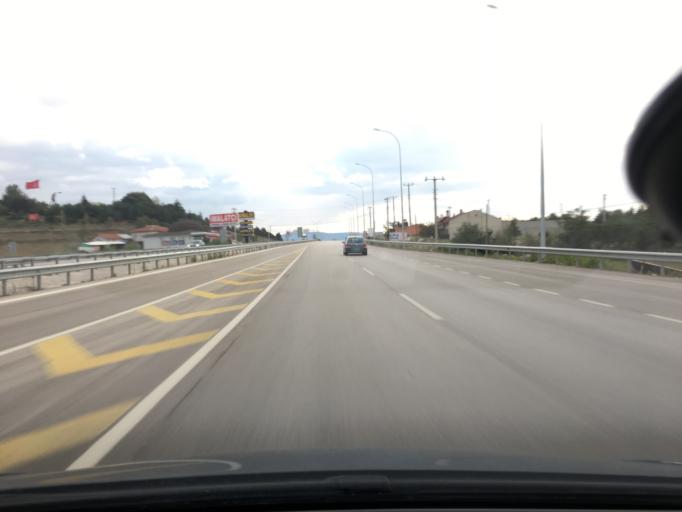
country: TR
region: Afyonkarahisar
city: Sincanli
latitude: 38.7951
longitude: 30.3877
